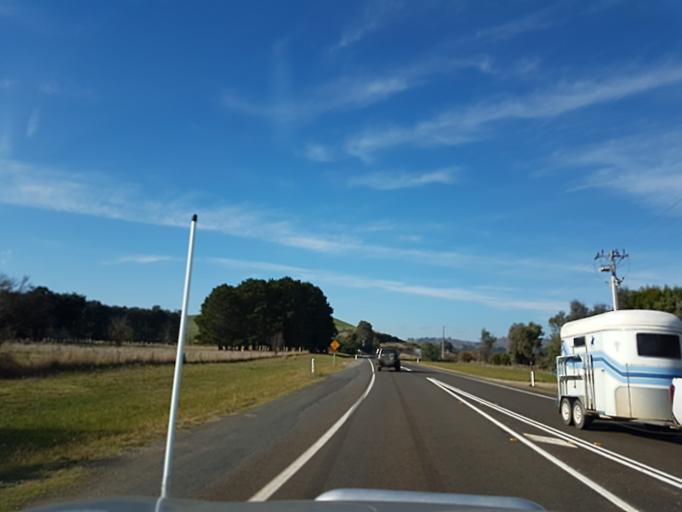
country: AU
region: Victoria
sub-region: Murrindindi
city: Alexandra
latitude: -37.1493
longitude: 145.5839
